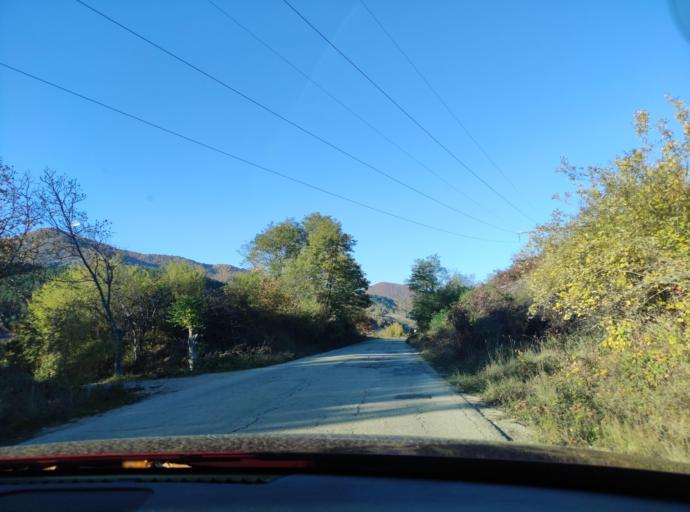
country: BG
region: Montana
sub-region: Obshtina Chiprovtsi
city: Chiprovtsi
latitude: 43.3814
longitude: 22.9184
